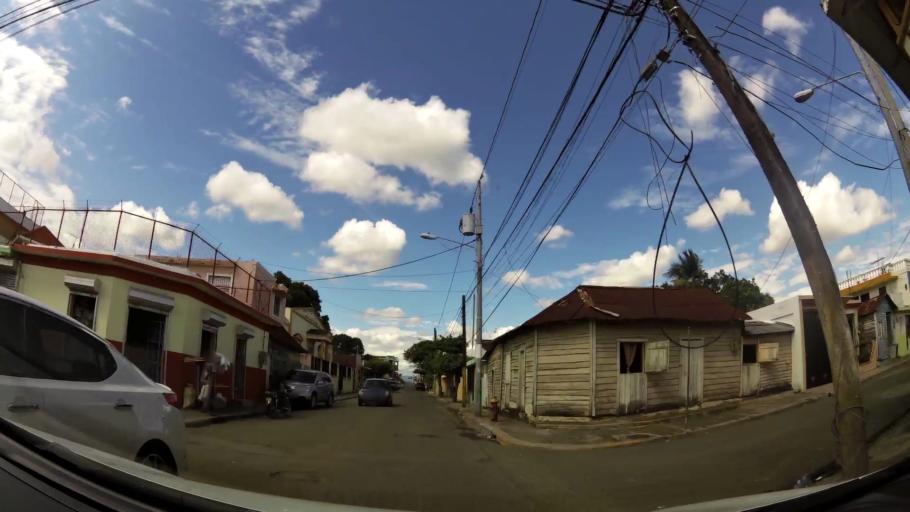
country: DO
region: La Vega
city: Concepcion de La Vega
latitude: 19.2214
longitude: -70.5343
